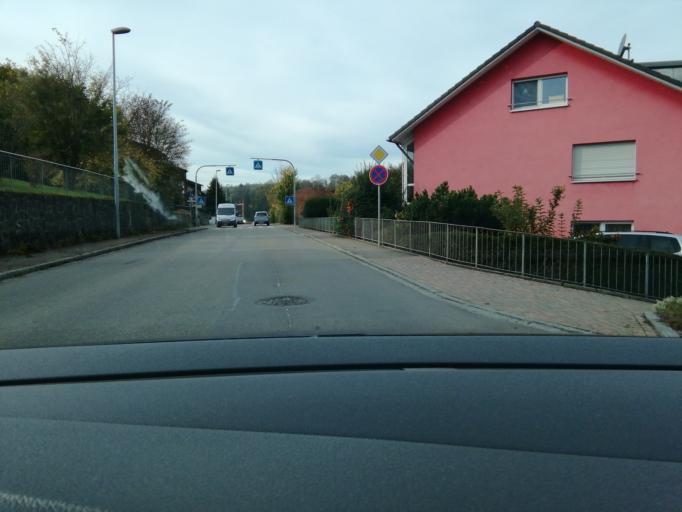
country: DE
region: Baden-Wuerttemberg
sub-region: Freiburg Region
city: Kandern
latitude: 47.7135
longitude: 7.6631
